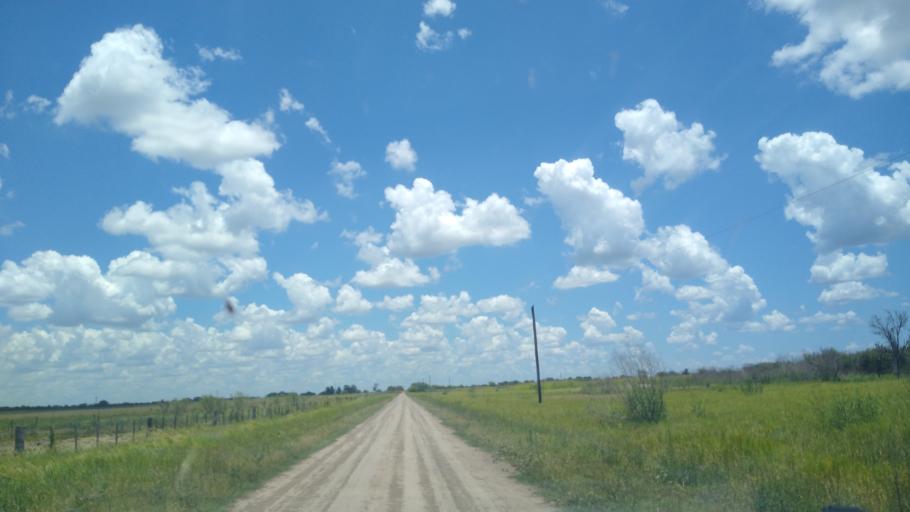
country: AR
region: Chaco
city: Presidencia Roque Saenz Pena
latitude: -26.7345
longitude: -60.3757
